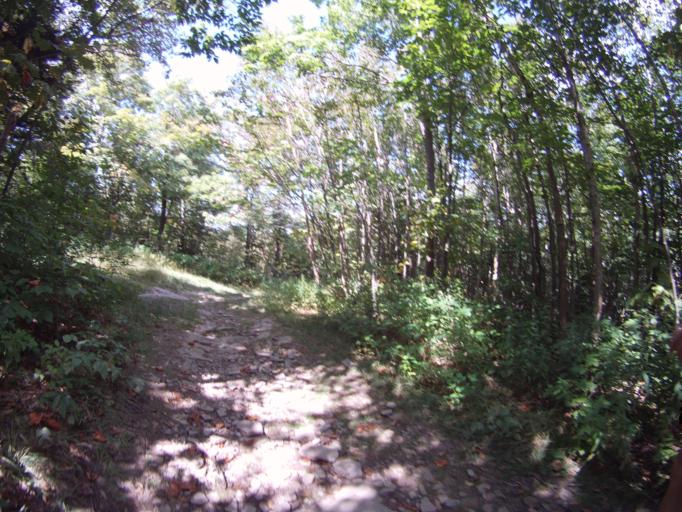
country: US
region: New York
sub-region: Ulster County
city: Woodstock
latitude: 42.1935
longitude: -74.2353
